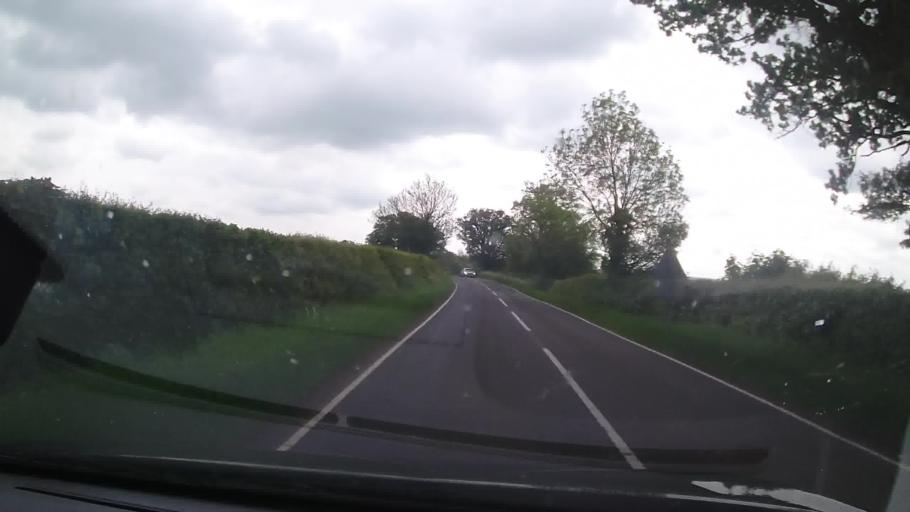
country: GB
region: England
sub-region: Shropshire
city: Wem
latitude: 52.8696
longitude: -2.7735
